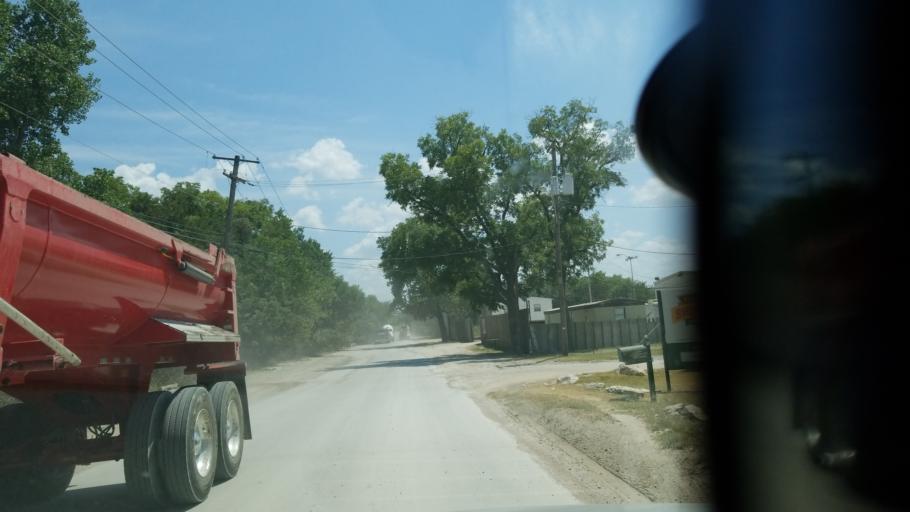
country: US
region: Texas
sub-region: Dallas County
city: Farmers Branch
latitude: 32.8745
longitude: -96.9198
